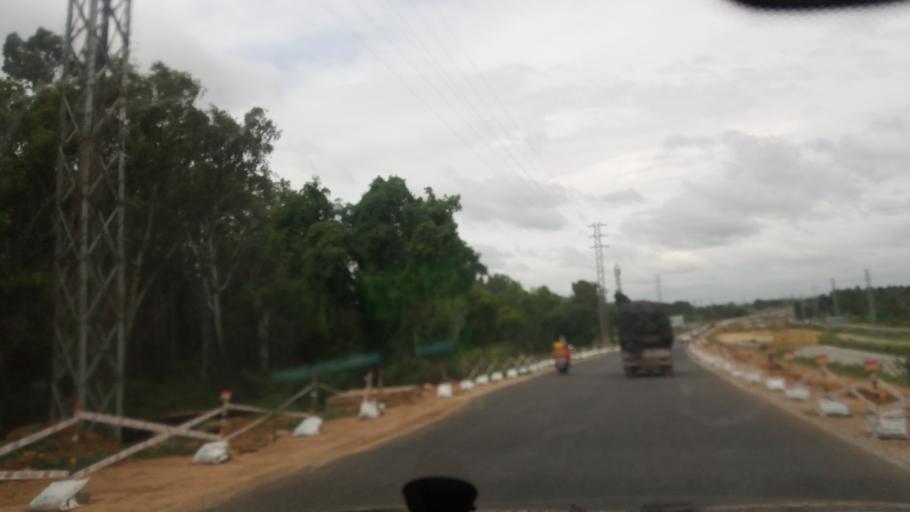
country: IN
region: Karnataka
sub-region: Mandya
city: Shrirangapattana
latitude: 12.4498
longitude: 76.7377
